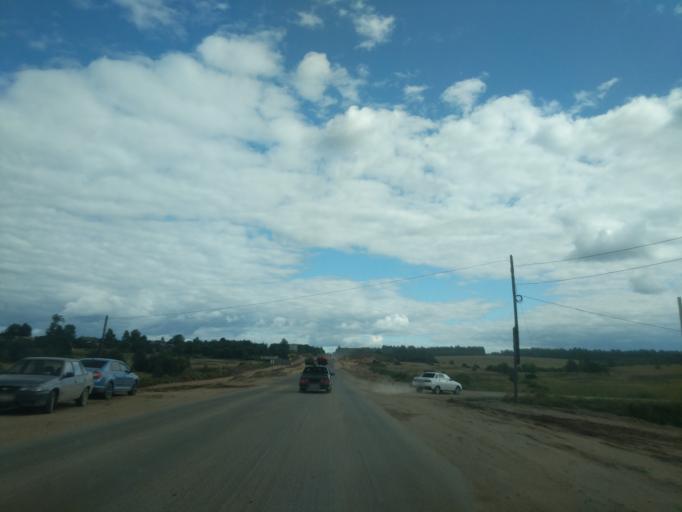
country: RU
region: Kostroma
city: Sudislavl'
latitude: 57.8763
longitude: 41.7309
